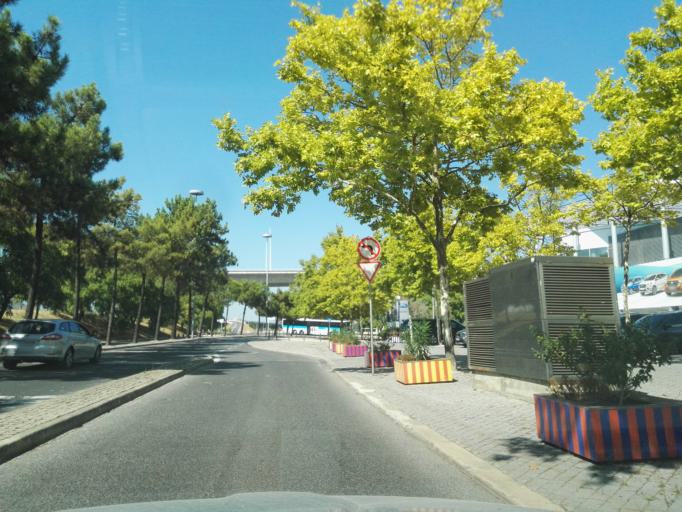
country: PT
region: Lisbon
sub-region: Loures
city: Moscavide
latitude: 38.7845
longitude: -9.1000
